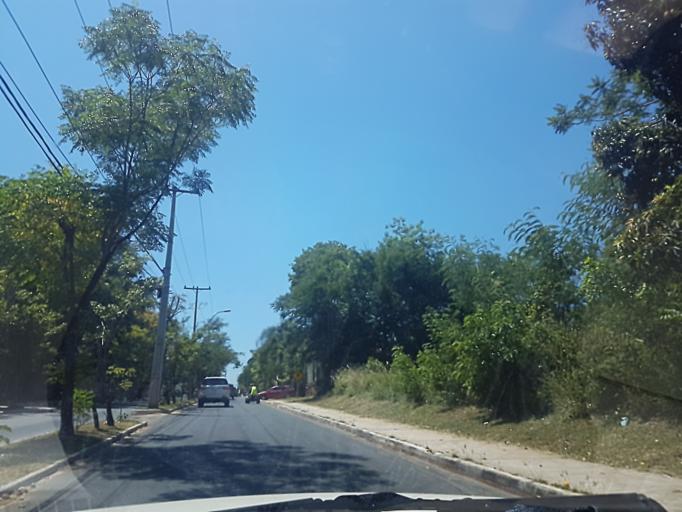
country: PY
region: Cordillera
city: San Bernardino
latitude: -25.3033
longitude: -57.2995
